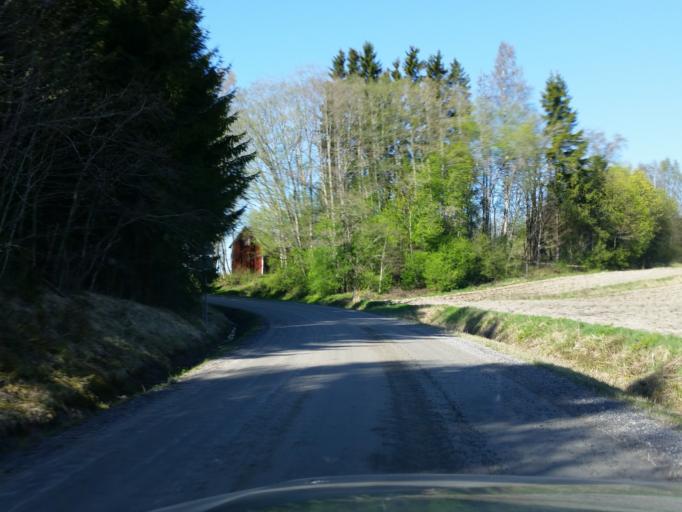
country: FI
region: Uusimaa
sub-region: Helsinki
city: Karjalohja
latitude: 60.1415
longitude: 23.7512
